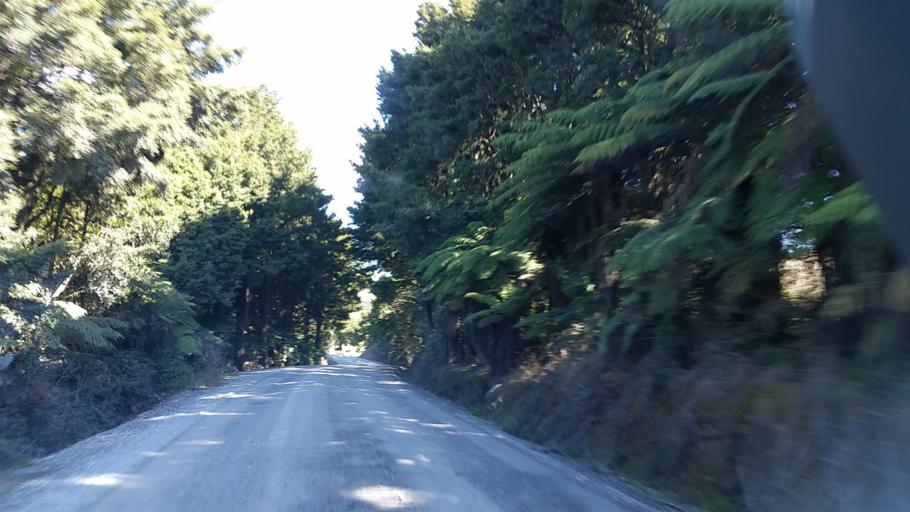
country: NZ
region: Northland
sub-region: Whangarei
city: Maungatapere
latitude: -35.6948
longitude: 174.2170
